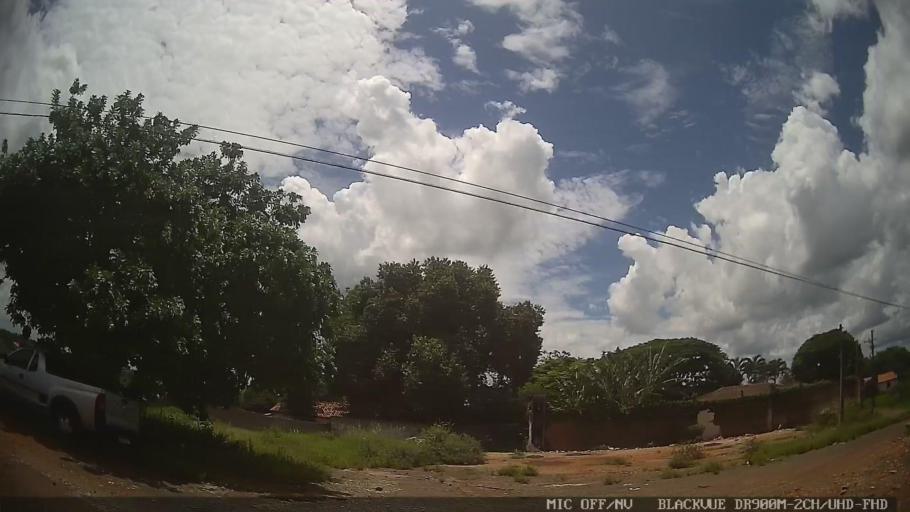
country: BR
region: Sao Paulo
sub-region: Laranjal Paulista
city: Laranjal Paulista
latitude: -23.0371
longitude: -47.8863
